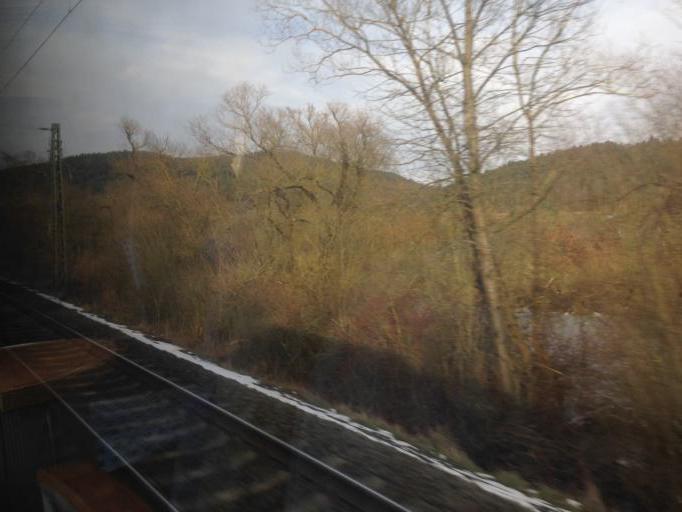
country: DE
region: Hesse
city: Herborn
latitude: 50.7099
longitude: 8.3059
